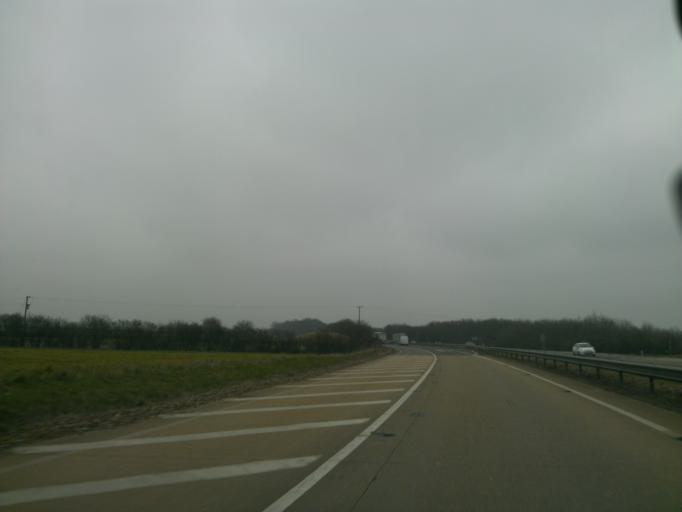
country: GB
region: England
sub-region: Essex
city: Great Bentley
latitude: 51.8854
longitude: 1.0552
